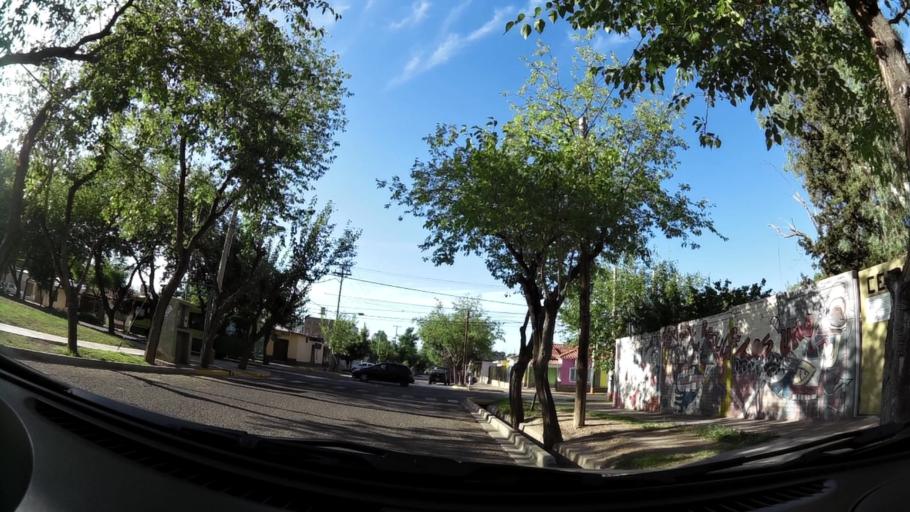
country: AR
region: Mendoza
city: Mendoza
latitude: -32.9006
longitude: -68.8207
